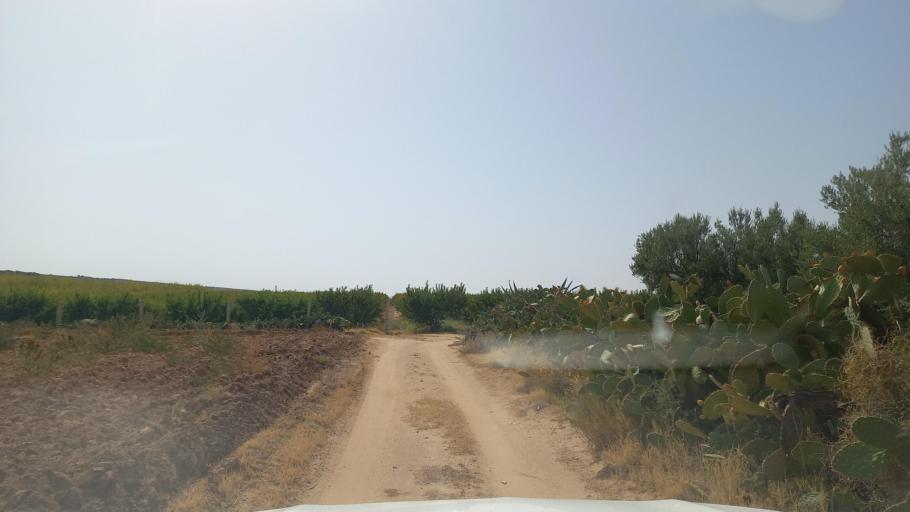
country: TN
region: Al Qasrayn
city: Kasserine
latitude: 35.2368
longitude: 9.0569
